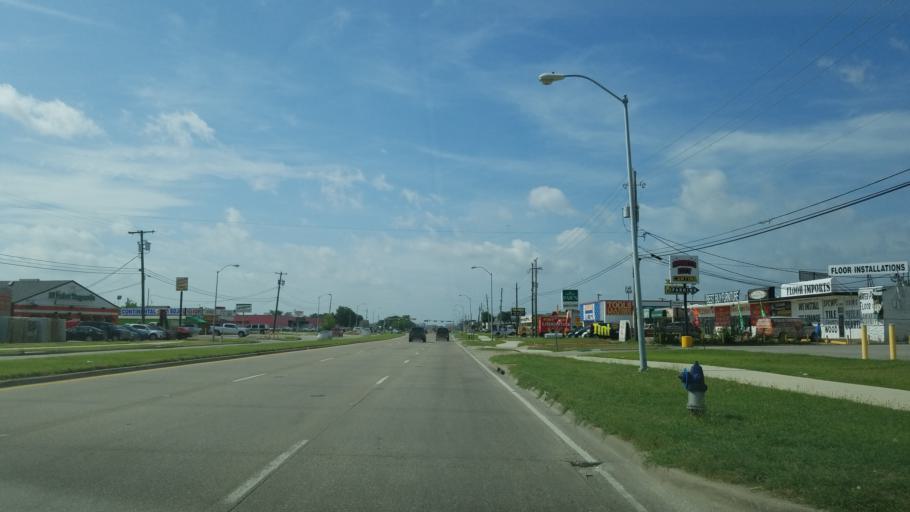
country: US
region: Texas
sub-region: Dallas County
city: Farmers Branch
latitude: 32.8768
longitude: -96.8846
